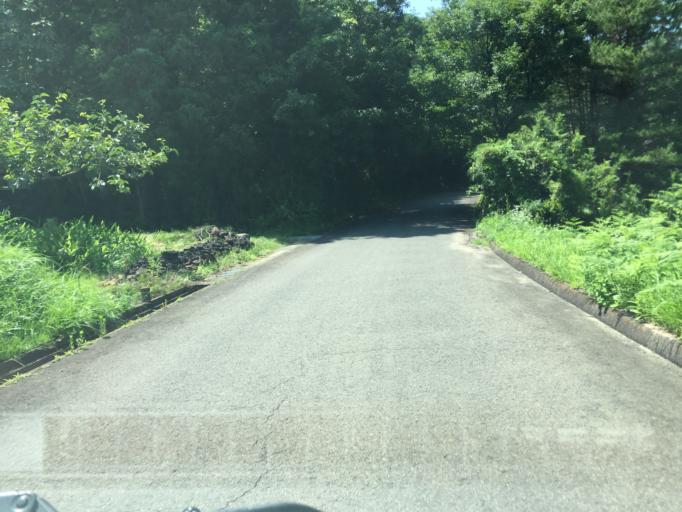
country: JP
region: Fukushima
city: Fukushima-shi
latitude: 37.7112
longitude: 140.4613
